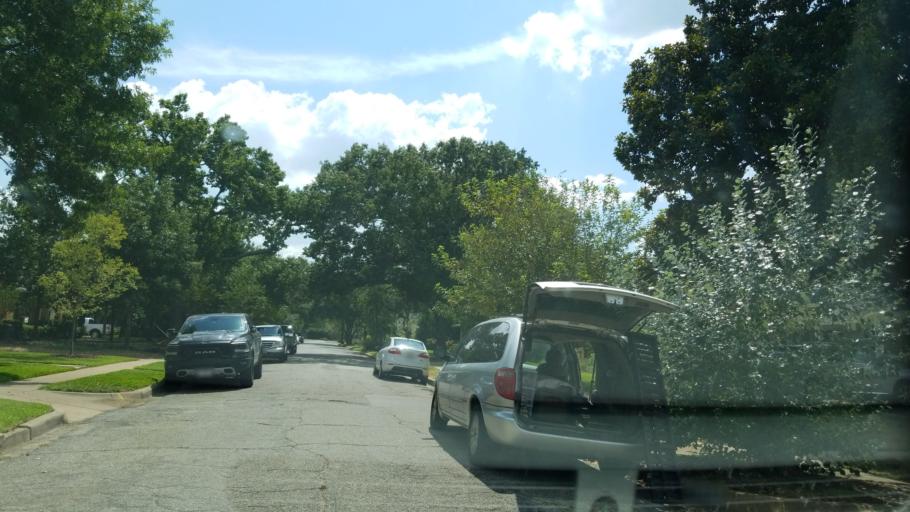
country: US
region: Texas
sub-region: Dallas County
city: Dallas
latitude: 32.7560
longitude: -96.8440
